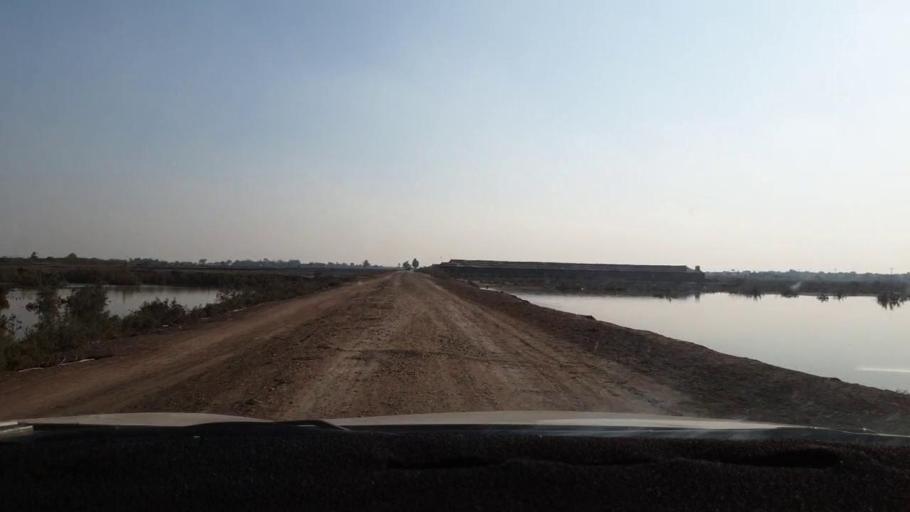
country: PK
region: Sindh
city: Berani
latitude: 25.7744
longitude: 68.7686
